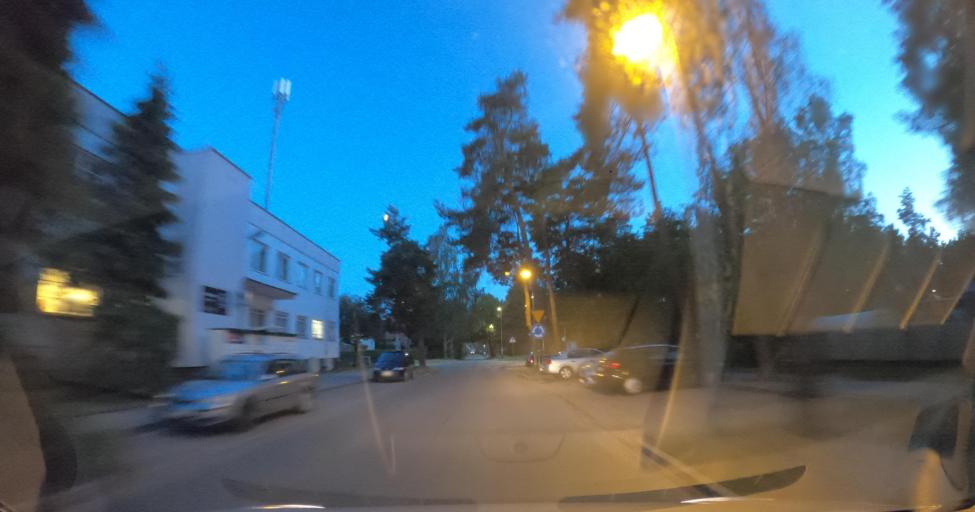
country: PL
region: Pomeranian Voivodeship
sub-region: Gdynia
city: Wielki Kack
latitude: 54.4289
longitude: 18.4683
